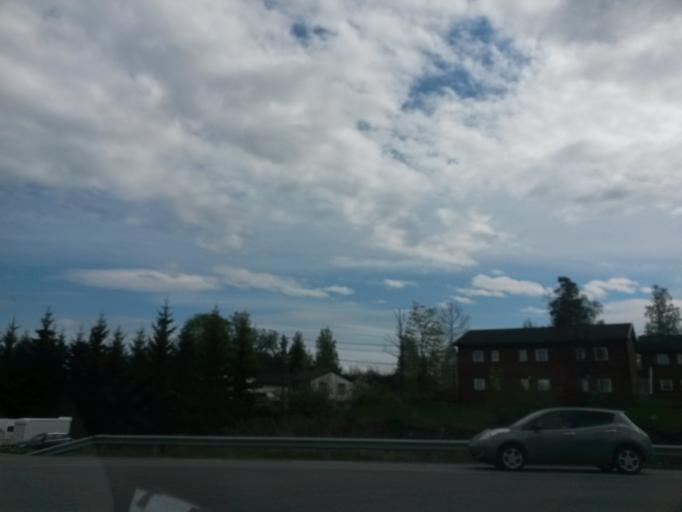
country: NO
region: Akershus
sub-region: Asker
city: Asker
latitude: 59.8275
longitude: 10.4371
